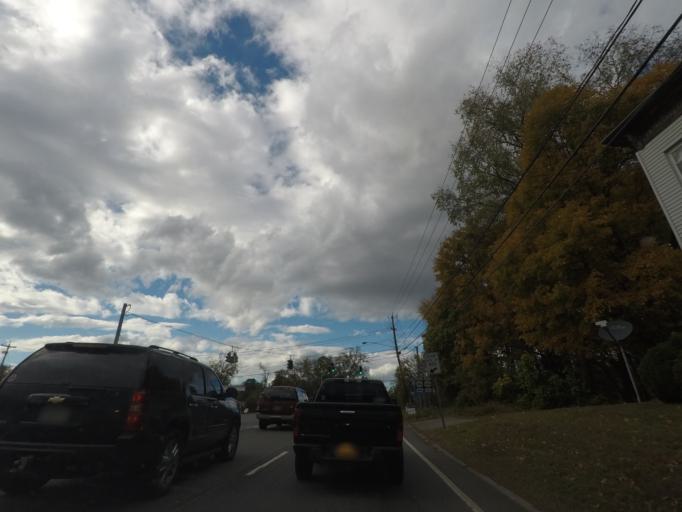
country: US
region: New York
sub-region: Albany County
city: Voorheesville
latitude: 42.7075
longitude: -73.9219
